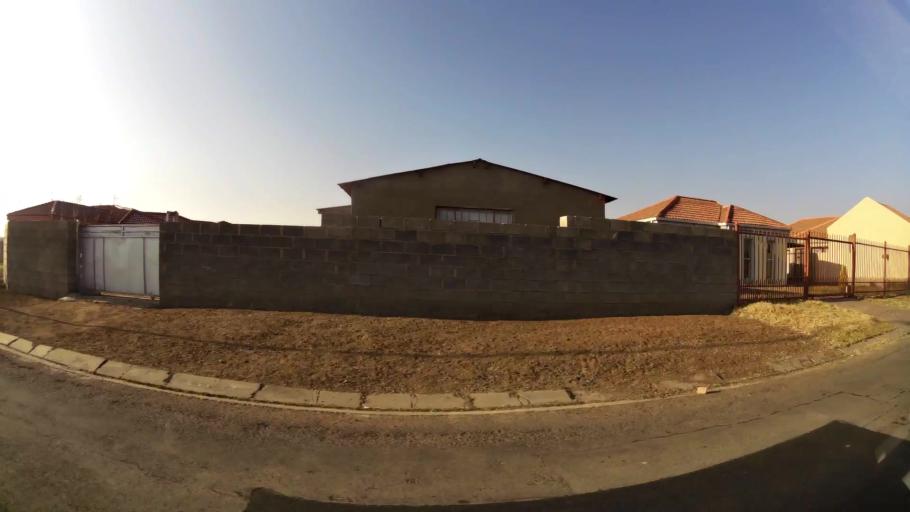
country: ZA
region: Orange Free State
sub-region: Mangaung Metropolitan Municipality
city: Bloemfontein
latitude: -29.1519
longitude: 26.2114
